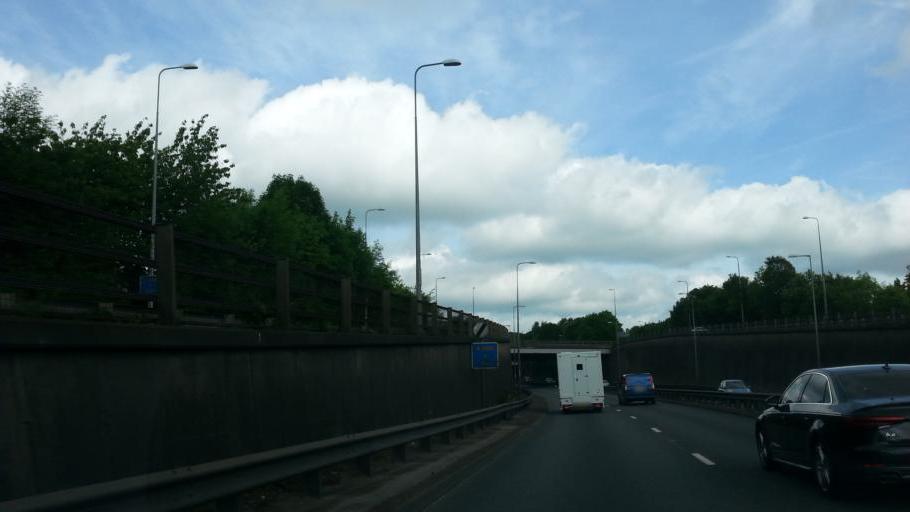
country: GB
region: England
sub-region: Staffordshire
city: Newcastle under Lyme
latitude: 53.0388
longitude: -2.2132
